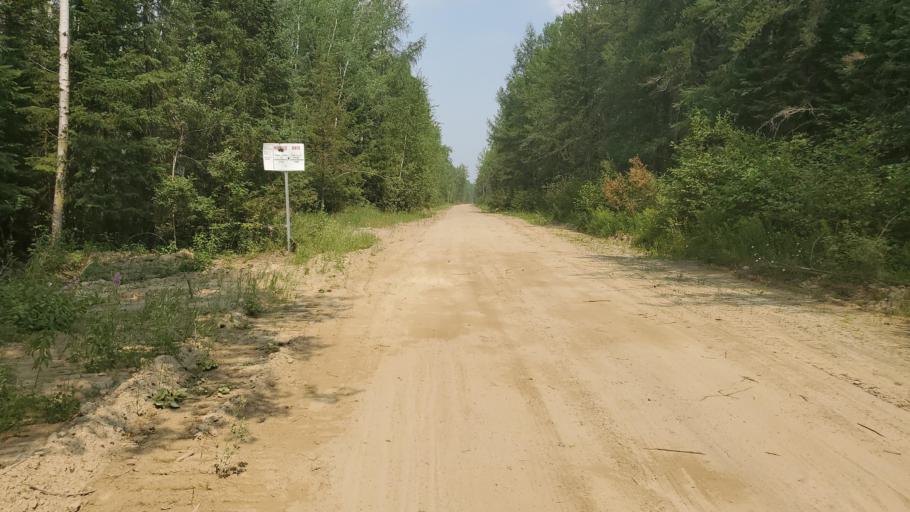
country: CA
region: Ontario
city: Greenstone
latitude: 49.7638
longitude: -87.7655
